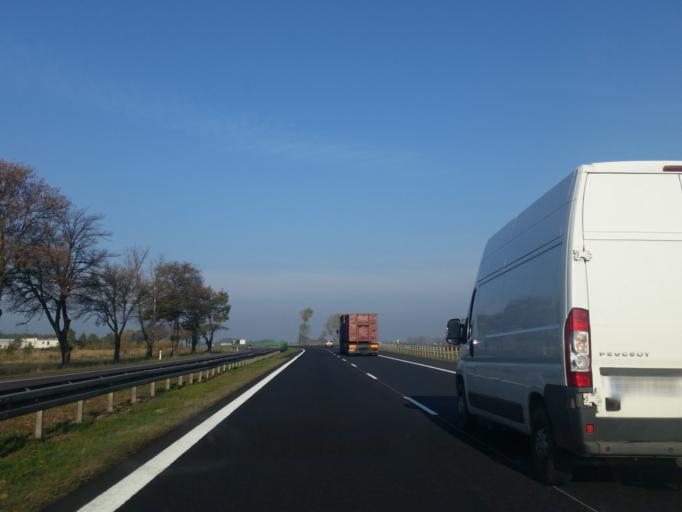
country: PL
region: Masovian Voivodeship
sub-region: Powiat plonski
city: Plonsk
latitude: 52.5906
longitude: 20.4475
